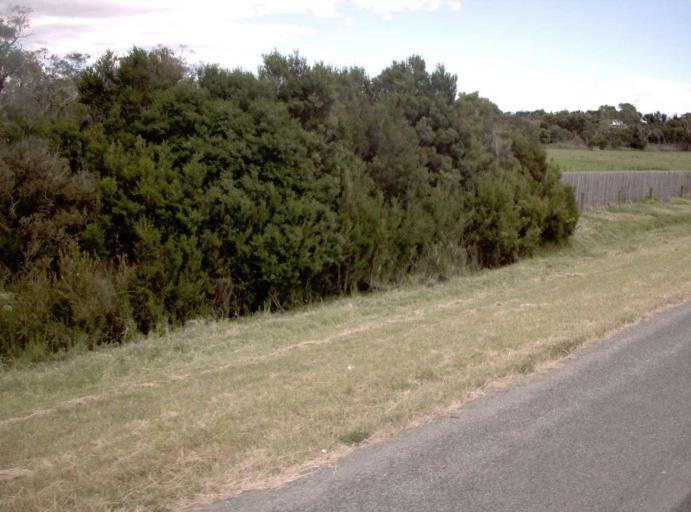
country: AU
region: Victoria
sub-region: Cardinia
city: Koo-Wee-Rup
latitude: -38.3248
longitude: 145.5432
